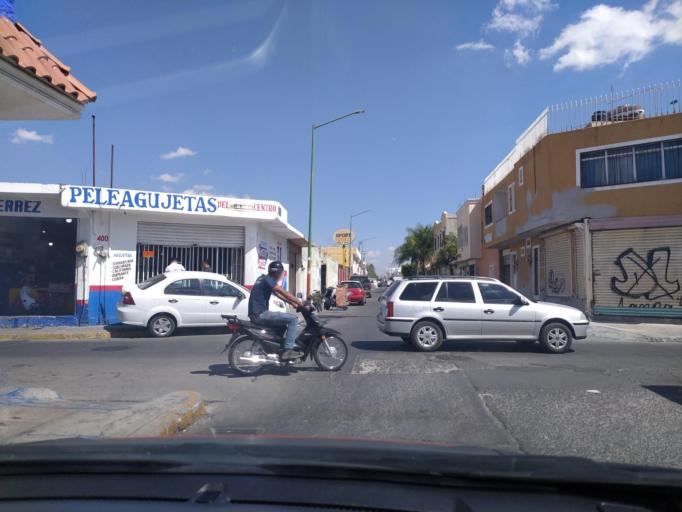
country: LA
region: Oudomxai
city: Muang La
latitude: 21.0240
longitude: 101.8546
